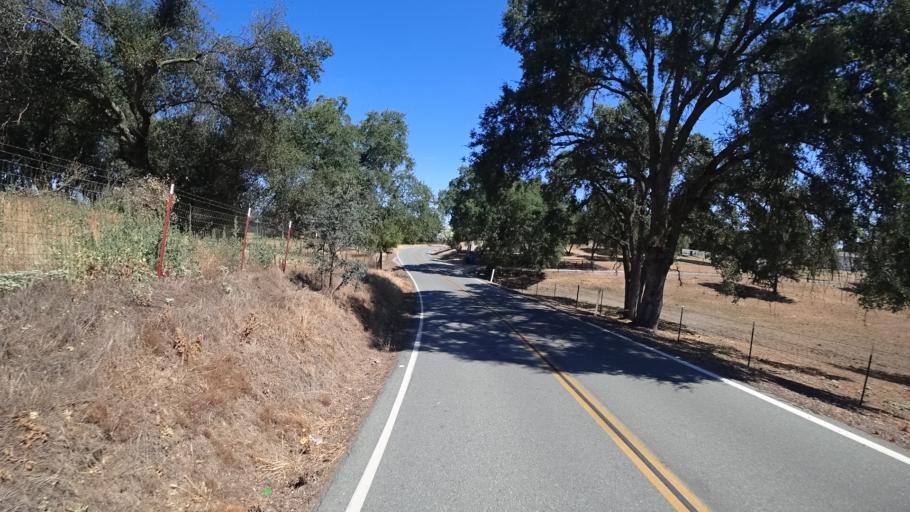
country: US
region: California
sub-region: Calaveras County
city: Rancho Calaveras
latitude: 38.1657
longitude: -120.9087
